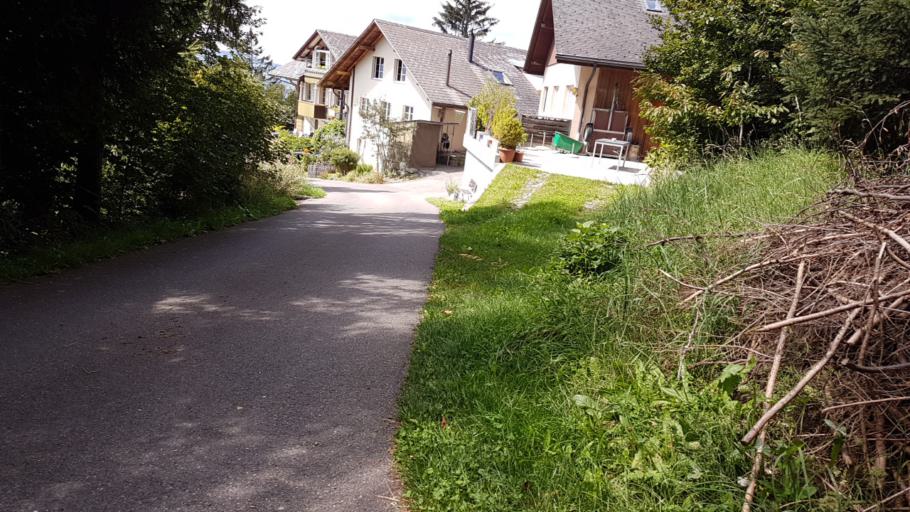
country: CH
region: Lucerne
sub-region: Entlebuch District
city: Oberdiessbach
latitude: 46.8220
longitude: 7.6387
